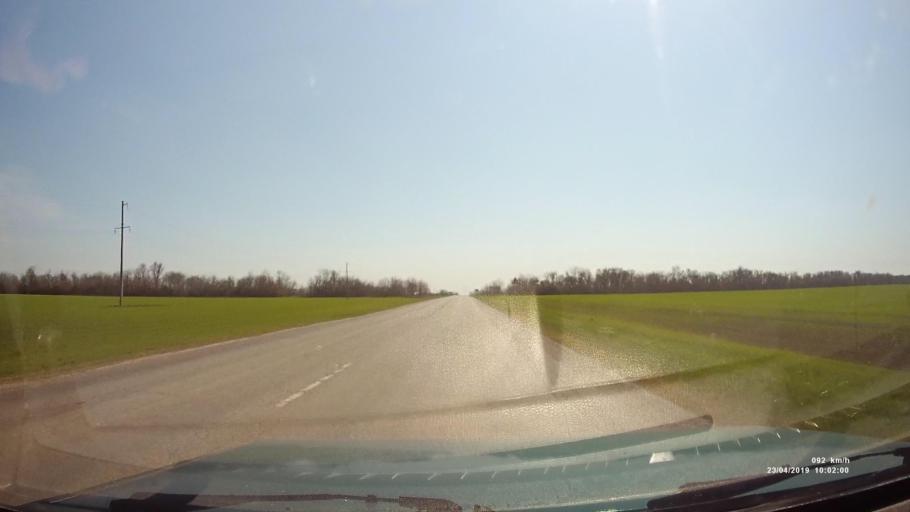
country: RU
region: Rostov
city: Sovetskoye
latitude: 46.7624
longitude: 42.1591
